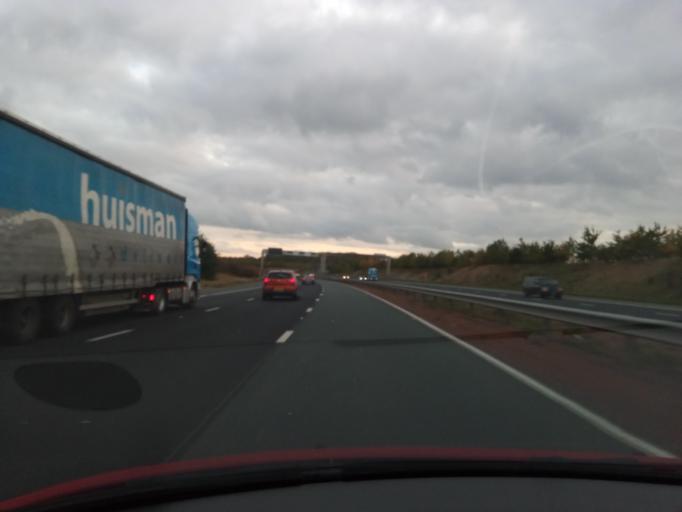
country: GB
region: England
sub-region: City and Borough of Leeds
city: Ledsham
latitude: 53.7876
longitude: -1.3220
